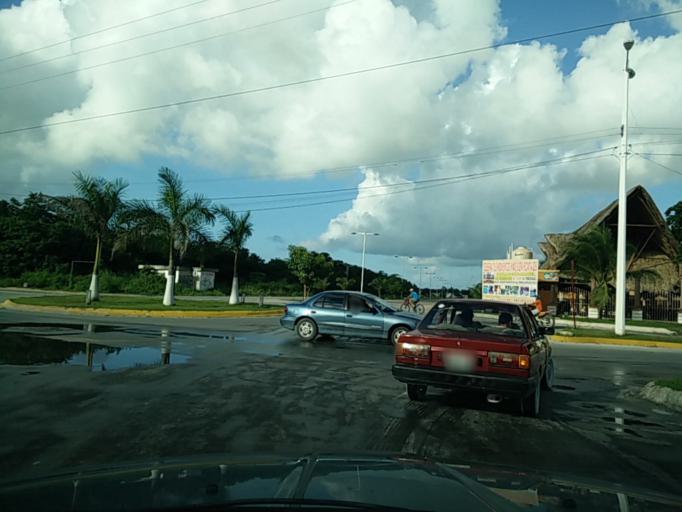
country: MX
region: Quintana Roo
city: San Miguel de Cozumel
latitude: 20.4940
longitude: -86.9289
